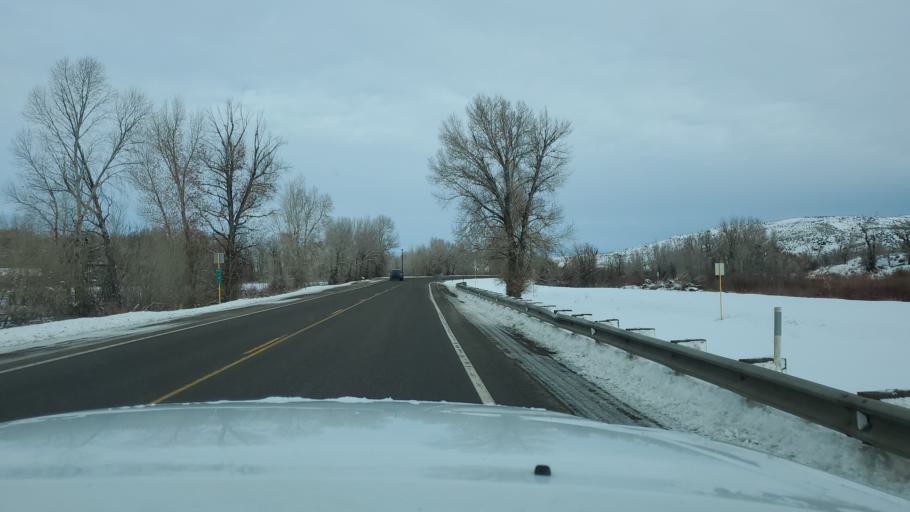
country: US
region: Colorado
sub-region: Routt County
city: Hayden
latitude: 40.5003
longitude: -107.3763
